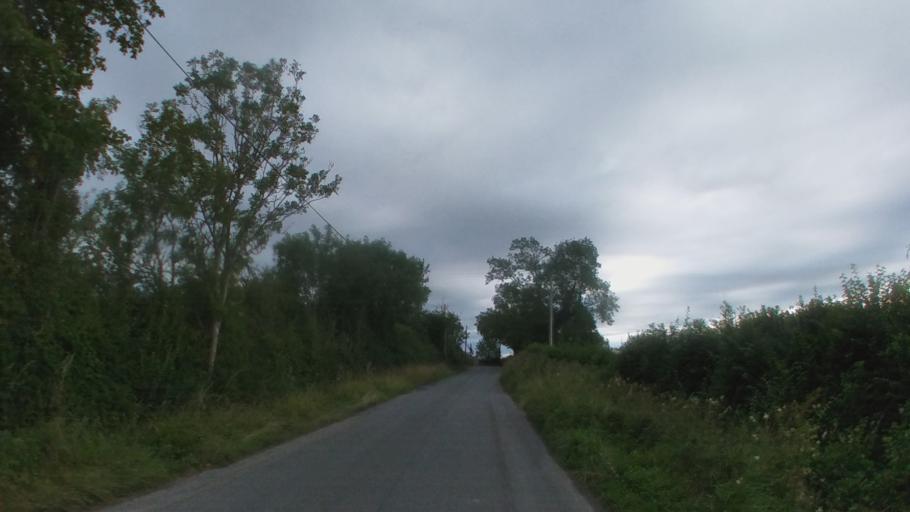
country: IE
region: Leinster
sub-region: Kilkenny
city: Kilkenny
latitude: 52.6907
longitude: -7.2163
